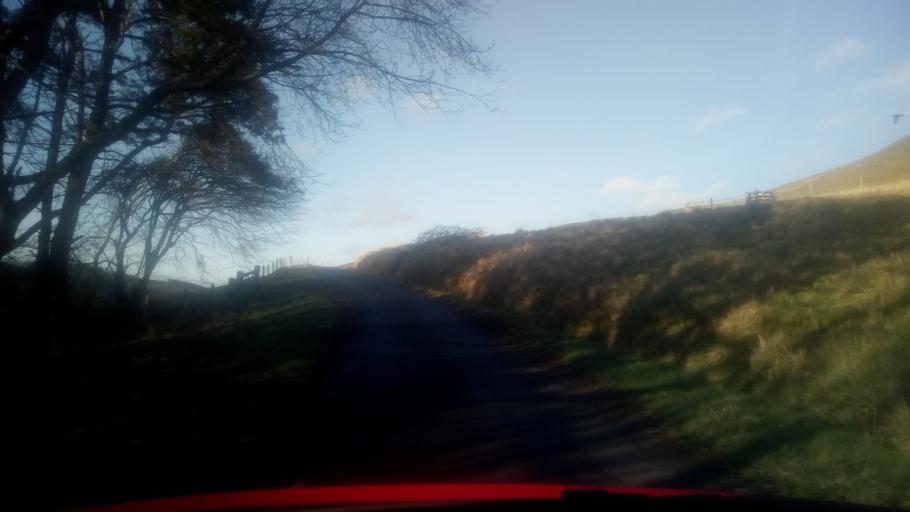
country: GB
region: Scotland
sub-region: The Scottish Borders
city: Kelso
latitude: 55.4383
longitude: -2.3634
